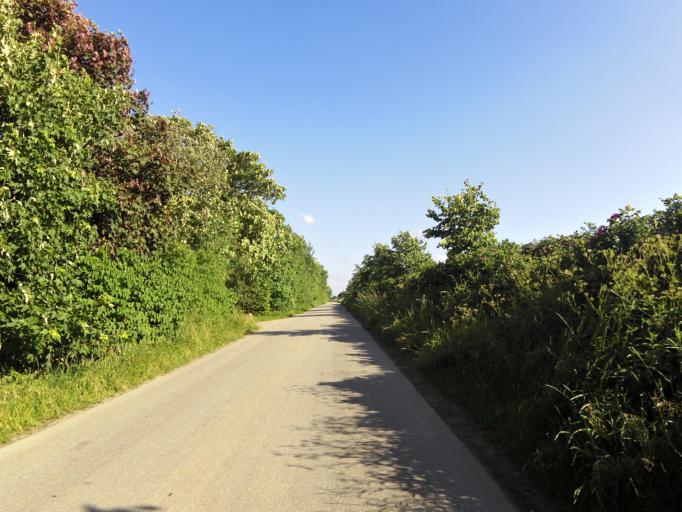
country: DK
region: South Denmark
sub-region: Vejen Kommune
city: Rodding
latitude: 55.3460
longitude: 9.1057
